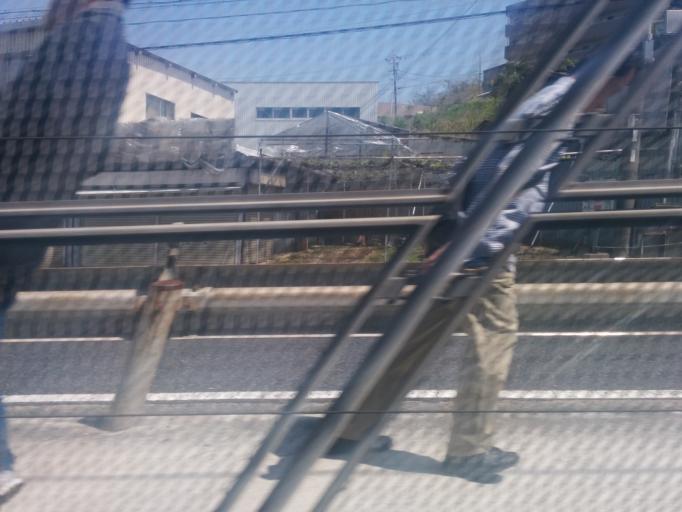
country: JP
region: Osaka
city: Kashihara
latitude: 34.5566
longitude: 135.6429
